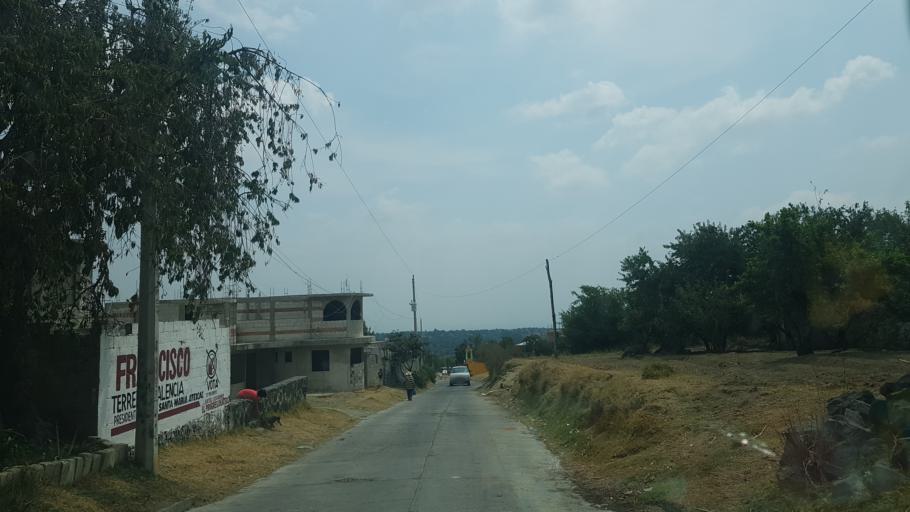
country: MX
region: Puebla
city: Domingo Arenas
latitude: 19.1369
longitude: -98.4836
